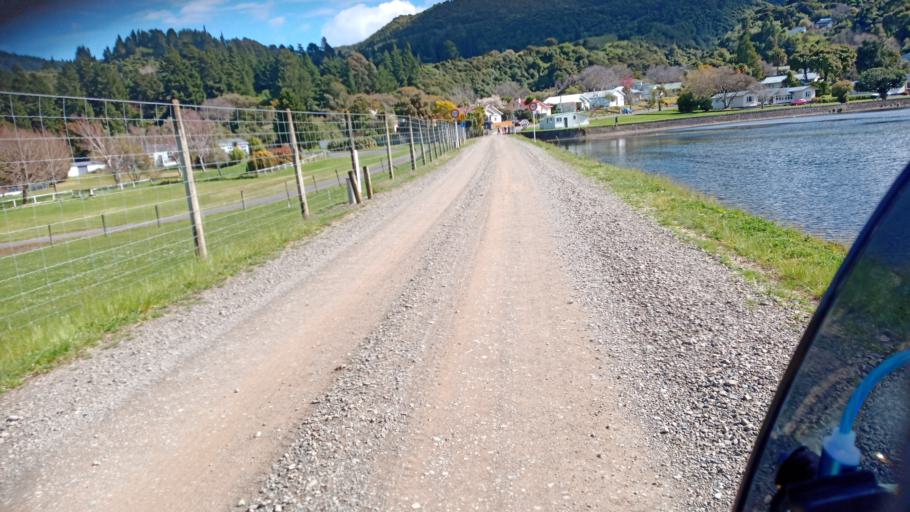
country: NZ
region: Hawke's Bay
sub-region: Wairoa District
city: Wairoa
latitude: -38.8138
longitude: 177.1506
